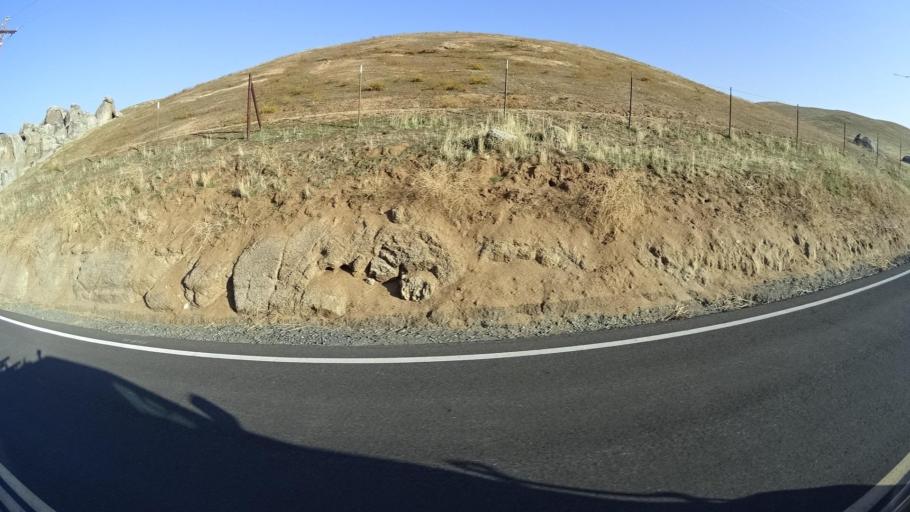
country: US
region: California
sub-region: Tulare County
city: Richgrove
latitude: 35.7425
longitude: -118.8992
